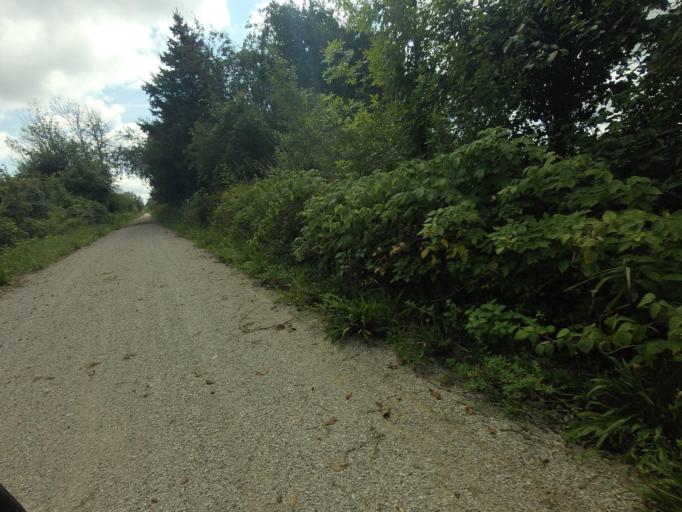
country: CA
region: Ontario
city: Huron East
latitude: 43.6224
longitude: -81.1594
